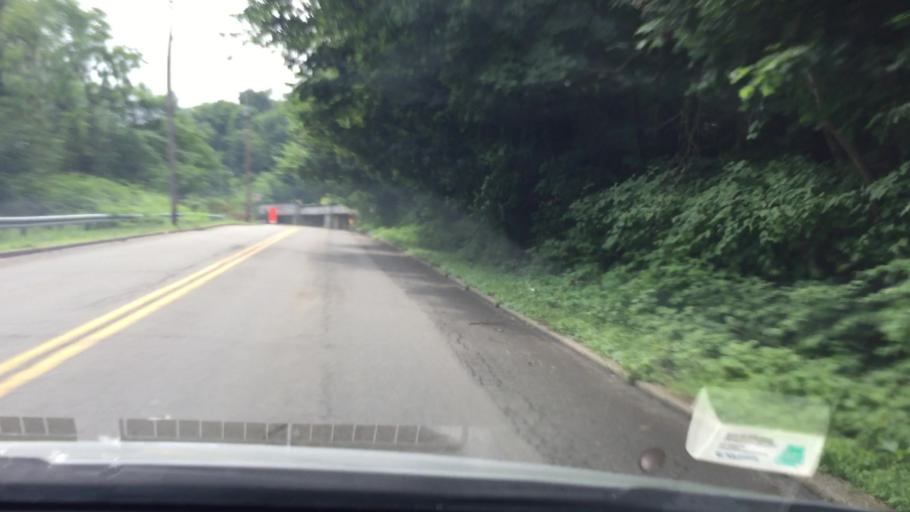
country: US
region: Pennsylvania
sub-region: Allegheny County
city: Green Tree
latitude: 40.4317
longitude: -80.0294
